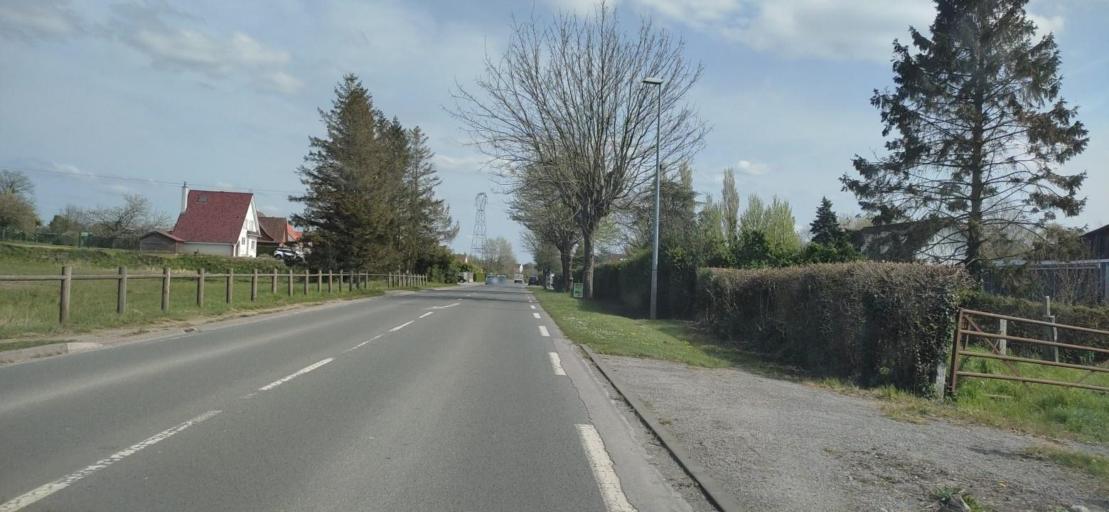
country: FR
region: Nord-Pas-de-Calais
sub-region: Departement du Pas-de-Calais
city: Montreuil
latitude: 50.4936
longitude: 1.7148
